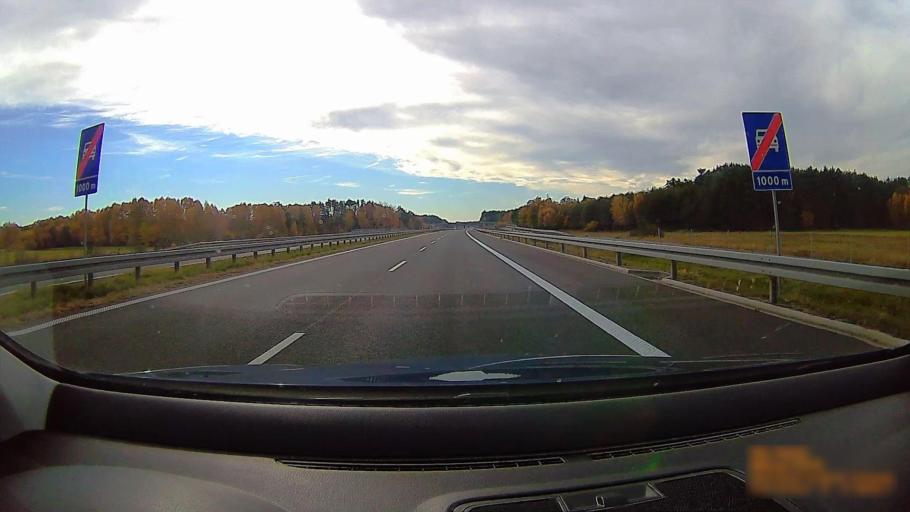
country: PL
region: Greater Poland Voivodeship
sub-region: Powiat ostrowski
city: Przygodzice
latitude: 51.5715
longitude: 17.8485
